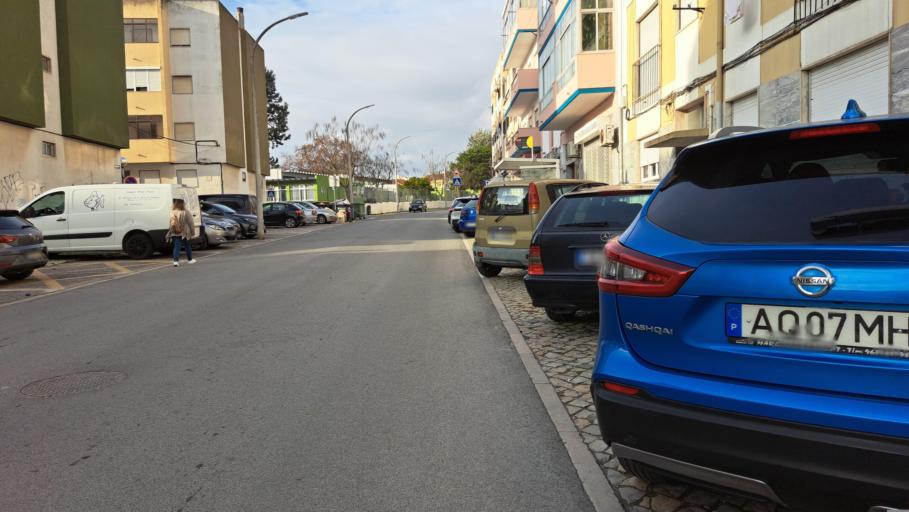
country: PT
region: Setubal
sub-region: Moita
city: Alhos Vedros
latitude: 38.6543
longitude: -9.0421
